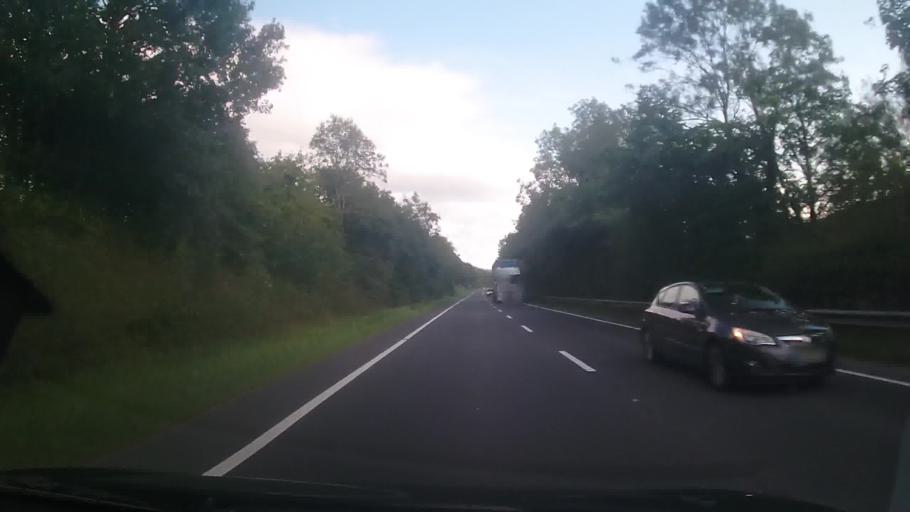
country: GB
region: England
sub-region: Shropshire
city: Craven Arms
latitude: 52.4184
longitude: -2.8188
